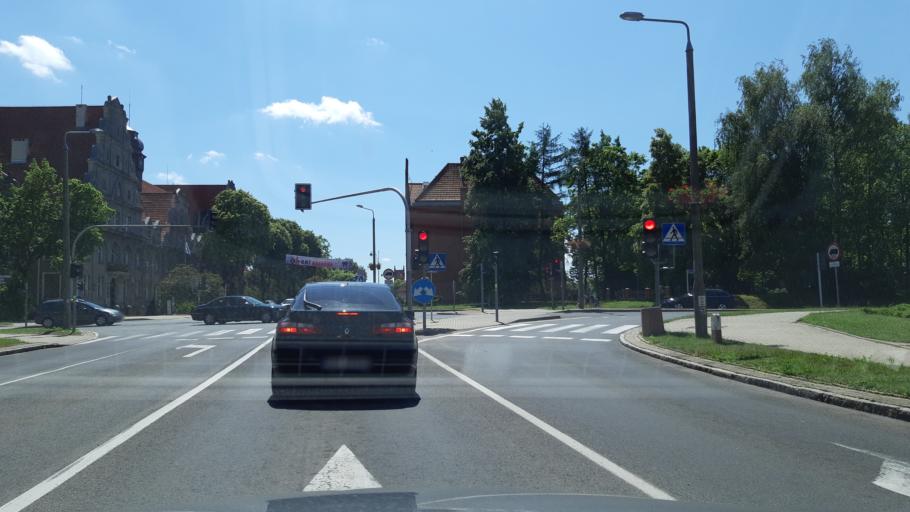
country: PL
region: Warmian-Masurian Voivodeship
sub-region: Powiat mragowski
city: Mragowo
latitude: 53.8774
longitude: 21.3039
